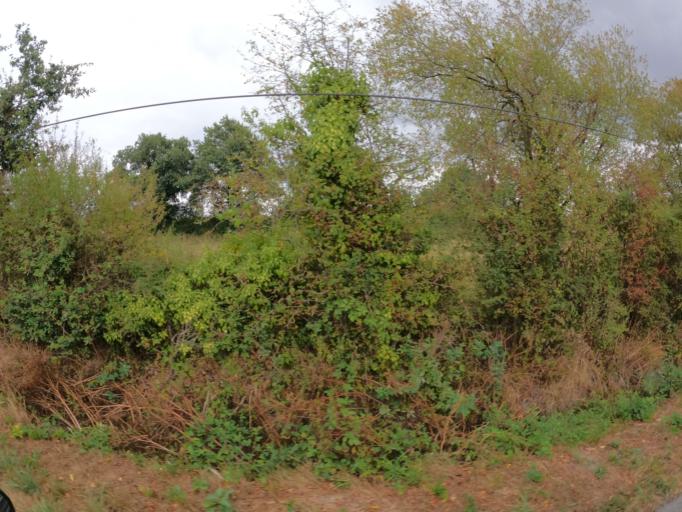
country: FR
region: Pays de la Loire
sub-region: Departement de la Vendee
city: Tiffauges
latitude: 46.9971
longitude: -1.0925
